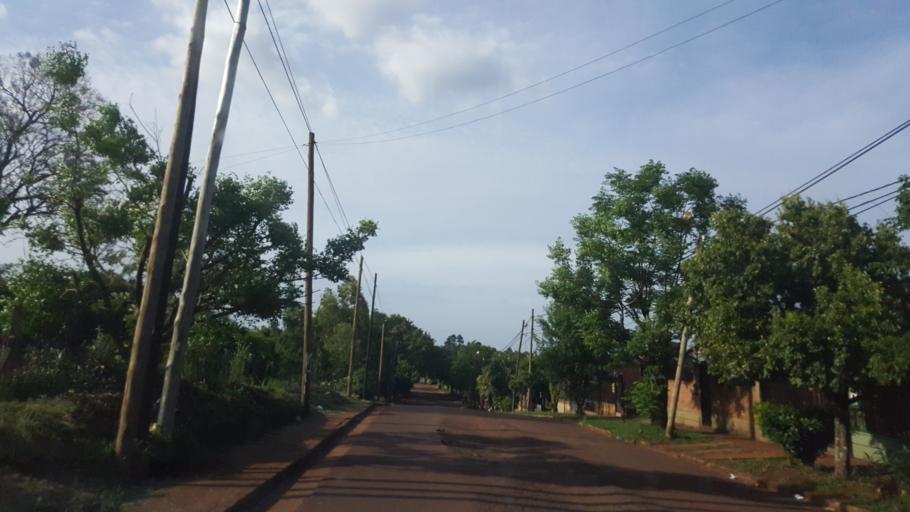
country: AR
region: Misiones
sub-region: Departamento de Capital
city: Posadas
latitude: -27.4253
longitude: -55.9246
